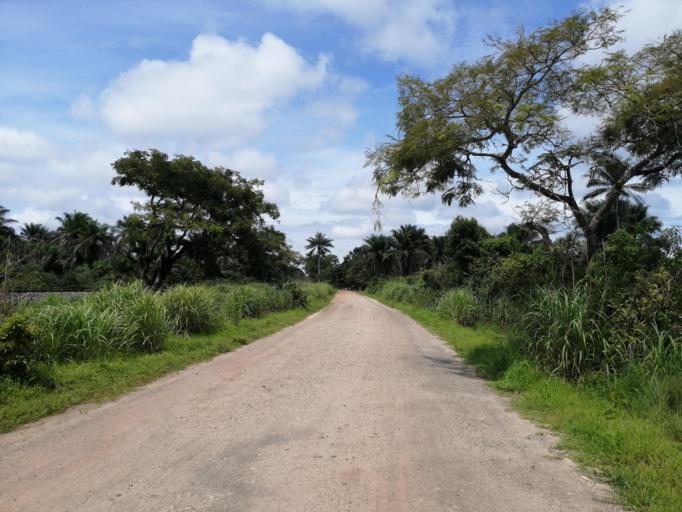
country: SL
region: Northern Province
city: Pepel
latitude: 8.6842
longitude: -12.9989
